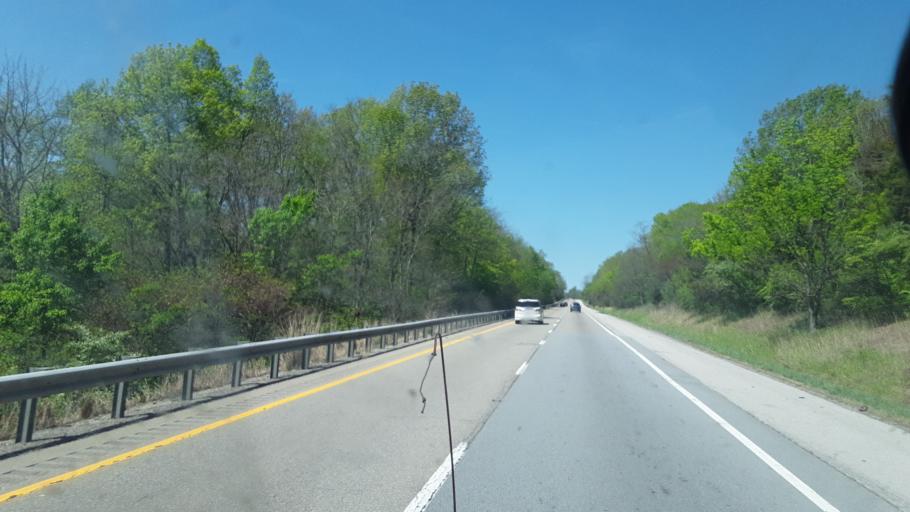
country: US
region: Indiana
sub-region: Switzerland County
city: Vevay
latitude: 38.6765
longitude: -84.9924
